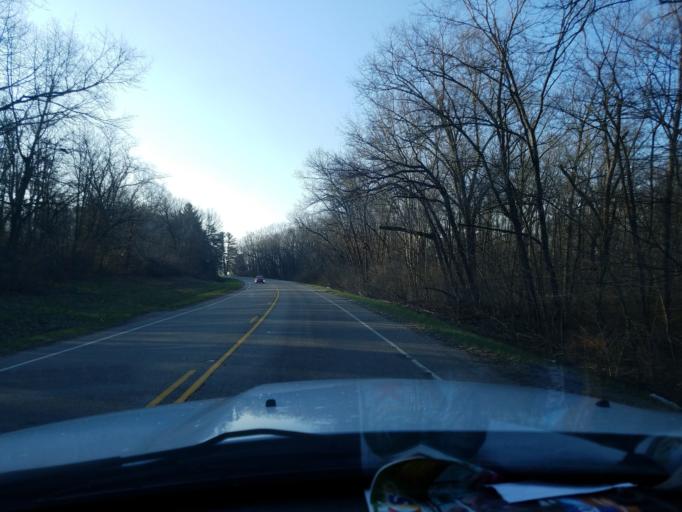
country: US
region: Indiana
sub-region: Vigo County
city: Seelyville
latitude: 39.4003
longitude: -87.3186
